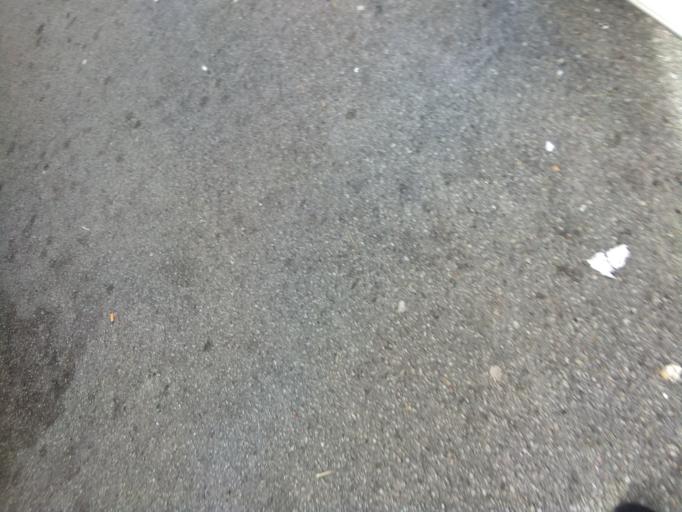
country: MY
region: Perak
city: Ipoh
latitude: 4.5912
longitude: 101.0824
